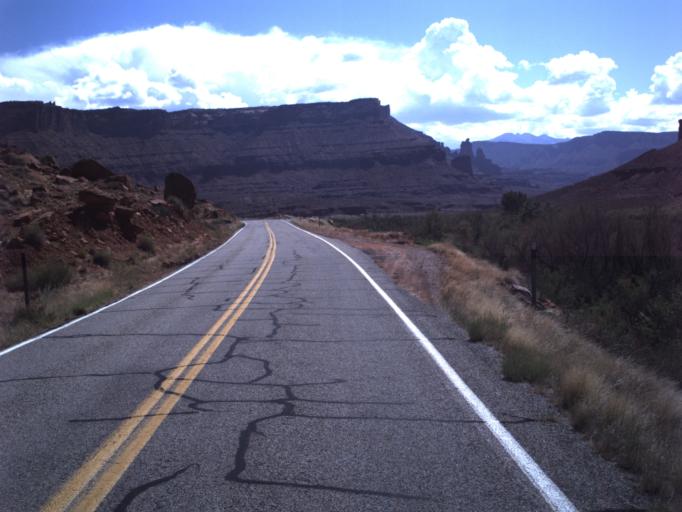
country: US
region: Utah
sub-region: Grand County
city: Moab
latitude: 38.7775
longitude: -109.3301
